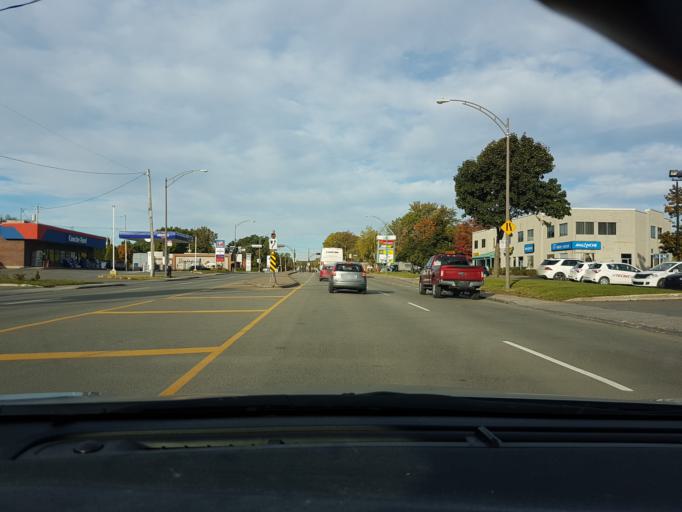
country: CA
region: Quebec
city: L'Ancienne-Lorette
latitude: 46.8062
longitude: -71.3150
